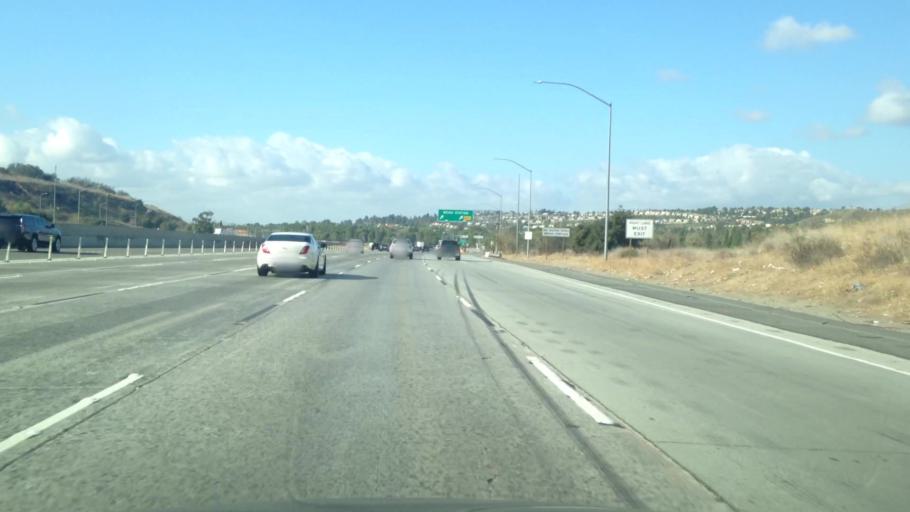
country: US
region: California
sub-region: Orange County
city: Yorba Linda
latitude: 33.8695
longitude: -117.7526
